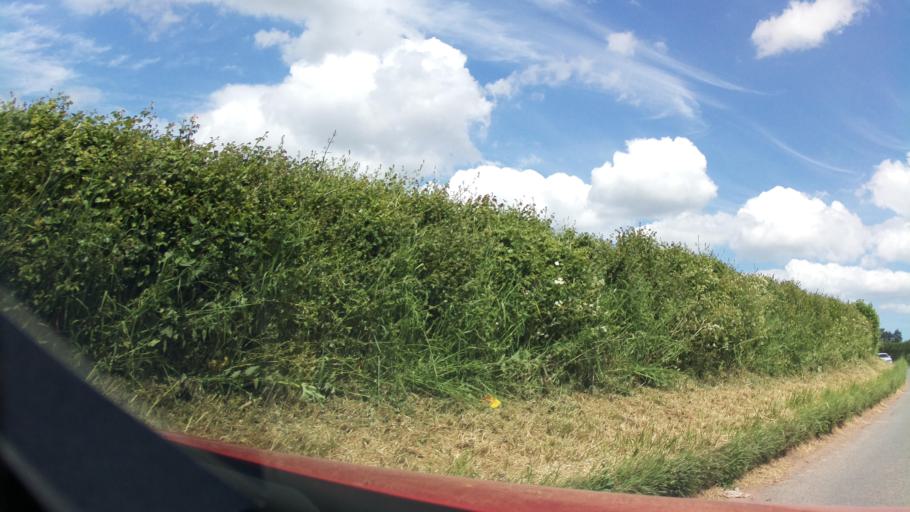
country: GB
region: England
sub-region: Herefordshire
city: Pencoyd
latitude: 51.9158
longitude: -2.6852
